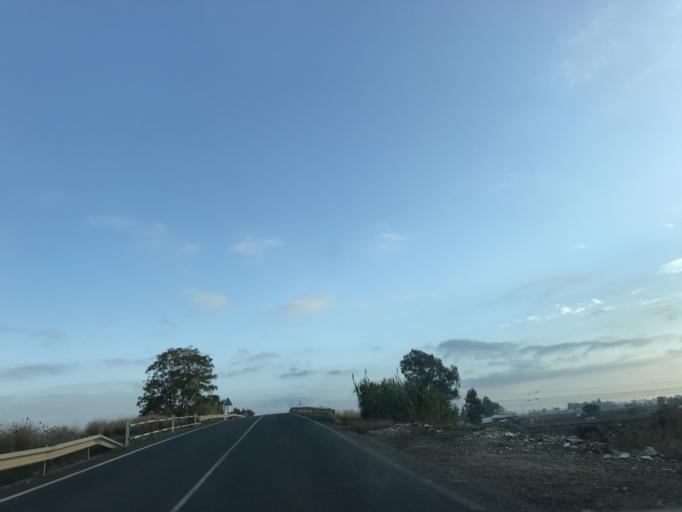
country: ES
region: Andalusia
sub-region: Provincia de Sevilla
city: Sevilla
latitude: 37.4205
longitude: -5.9499
